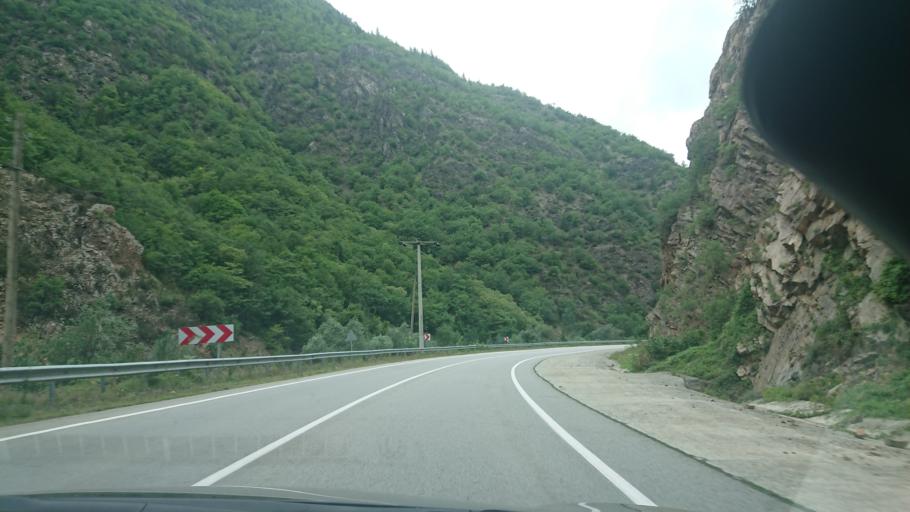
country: TR
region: Gumushane
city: Kurtun
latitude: 40.7271
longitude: 39.0171
